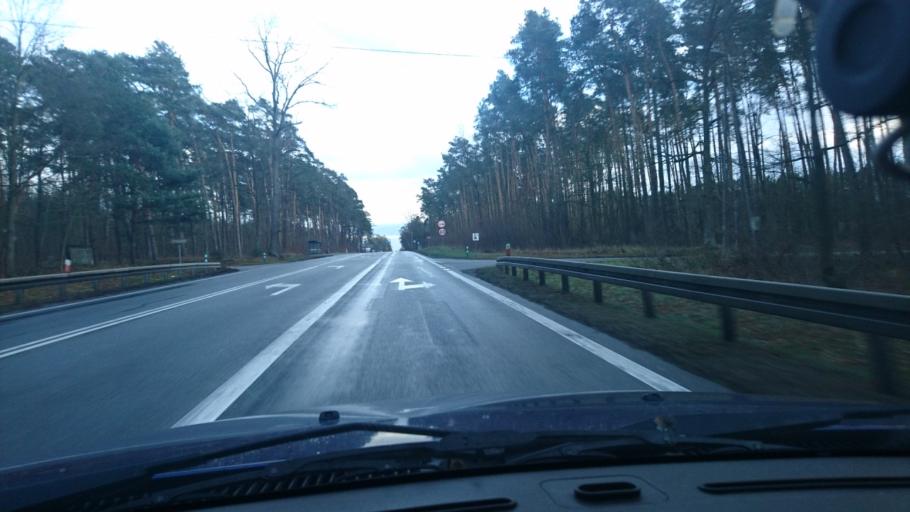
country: PL
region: Greater Poland Voivodeship
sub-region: Powiat kepinski
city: Kepno
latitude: 51.3263
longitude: 17.9641
